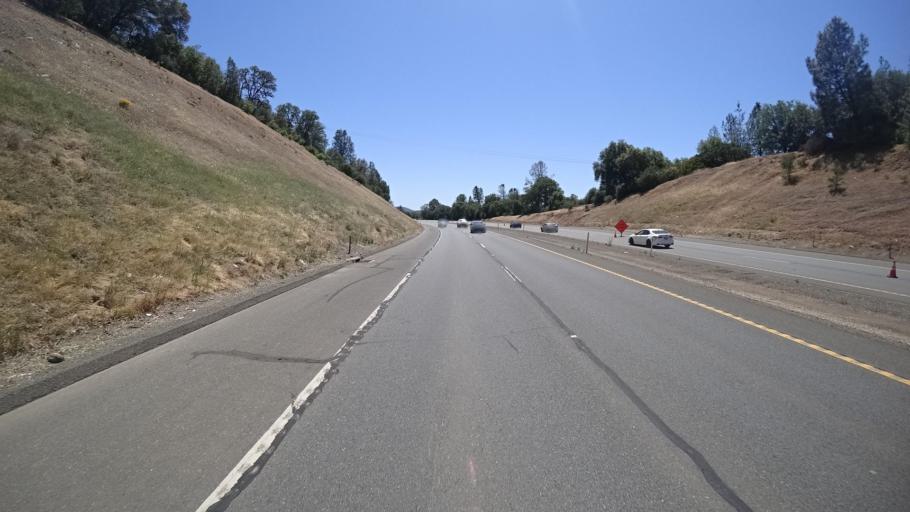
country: US
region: California
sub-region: Lake County
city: Clearlake
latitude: 38.9405
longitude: -122.6234
